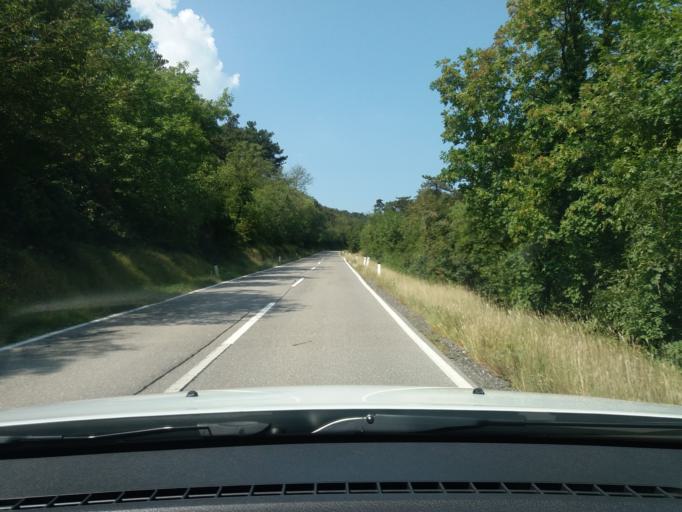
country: SI
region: Miren-Kostanjevica
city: Miren
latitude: 45.8811
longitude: 13.5995
